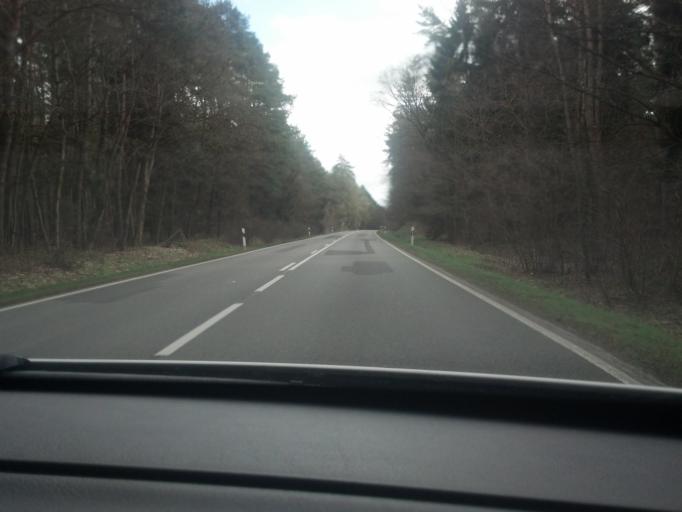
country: DE
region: Mecklenburg-Vorpommern
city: Plau am See
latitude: 53.3827
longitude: 12.3208
